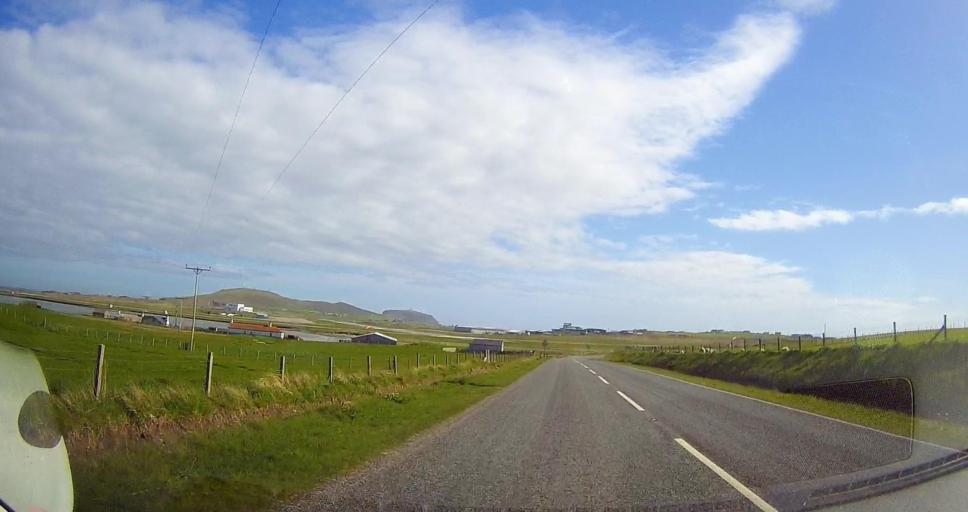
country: GB
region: Scotland
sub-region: Shetland Islands
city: Sandwick
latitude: 59.8862
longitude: -1.3029
